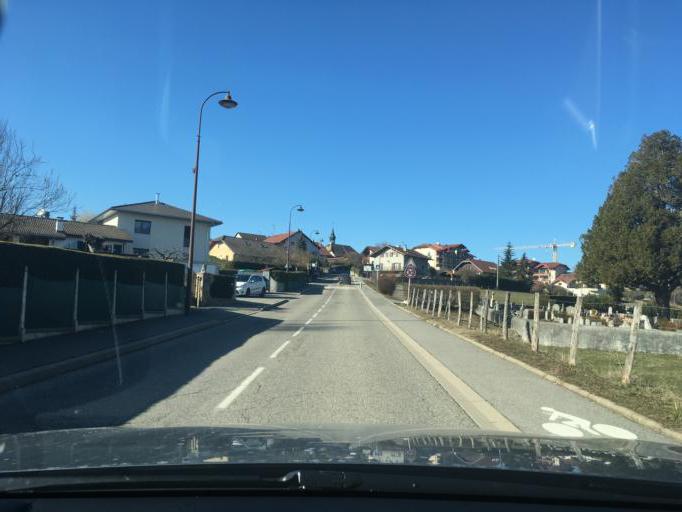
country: FR
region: Rhone-Alpes
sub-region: Departement de la Haute-Savoie
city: Cranves-Sales
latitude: 46.1845
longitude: 6.2939
